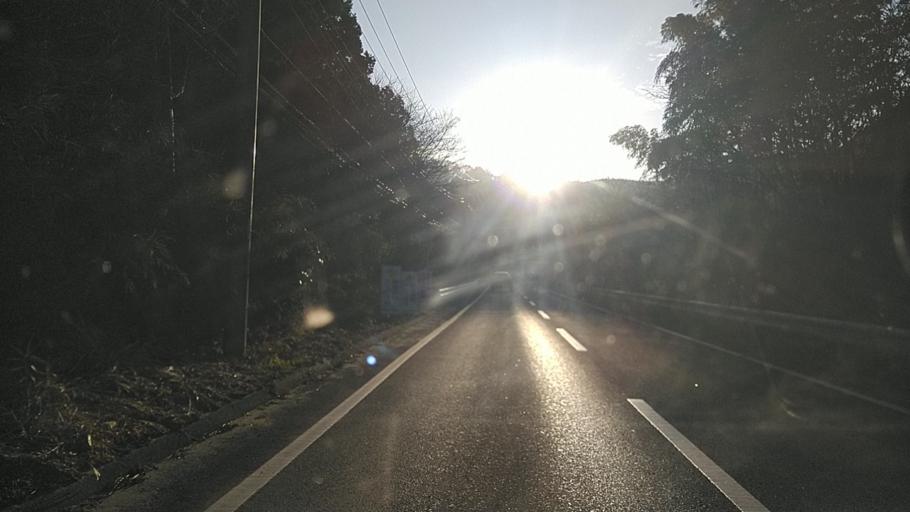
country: JP
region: Chiba
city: Kimitsu
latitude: 35.2701
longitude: 139.9210
